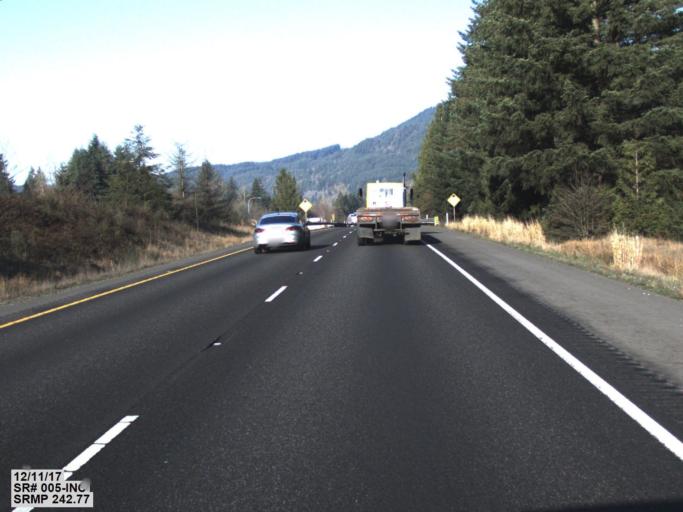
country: US
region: Washington
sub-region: Whatcom County
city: Sudden Valley
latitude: 48.6470
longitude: -122.3651
